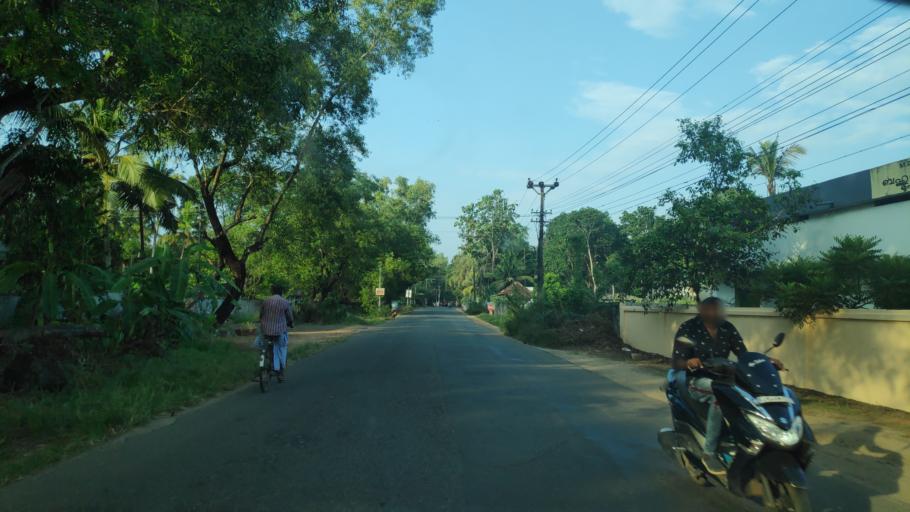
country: IN
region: Kerala
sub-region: Alappuzha
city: Shertallai
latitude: 9.6112
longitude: 76.3620
